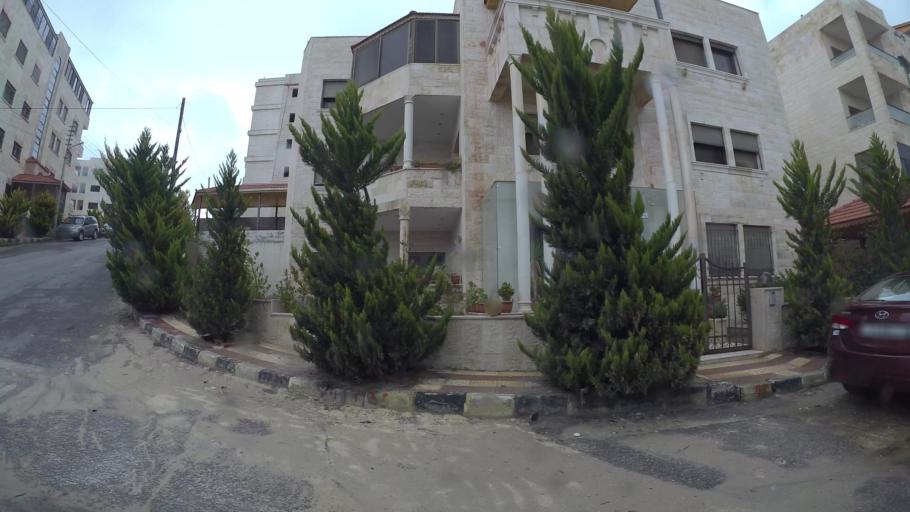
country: JO
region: Amman
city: Al Jubayhah
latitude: 32.0610
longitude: 35.8882
